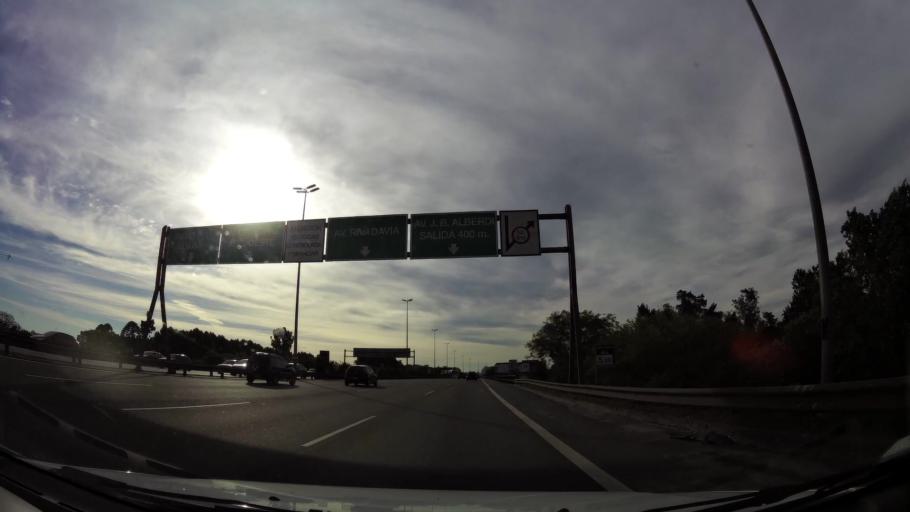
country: AR
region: Buenos Aires F.D.
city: Villa Lugano
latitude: -34.6470
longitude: -58.4819
